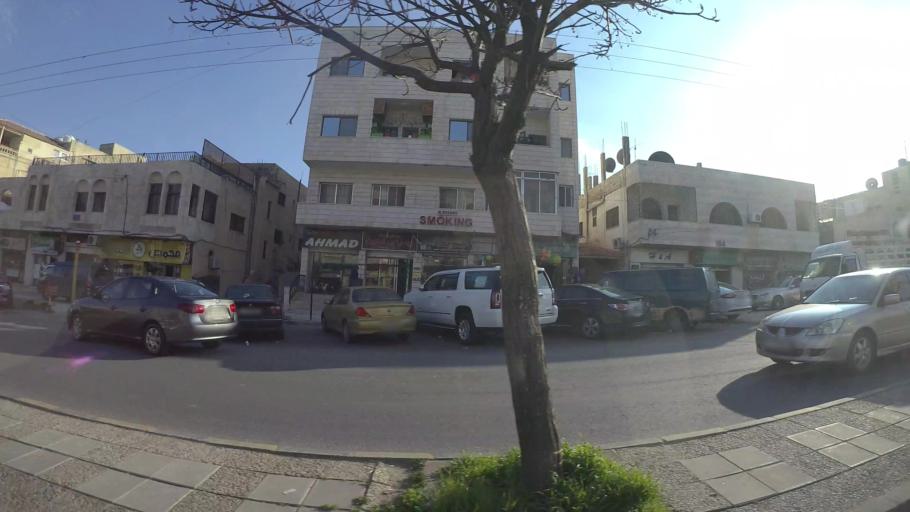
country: JO
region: Amman
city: Amman
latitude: 31.9749
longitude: 35.9626
